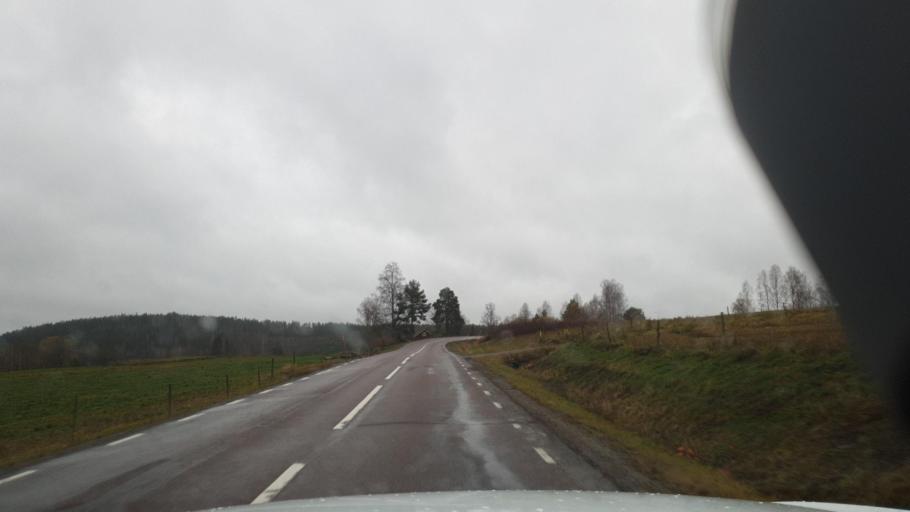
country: SE
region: Vaermland
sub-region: Sunne Kommun
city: Sunne
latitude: 59.6663
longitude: 13.0083
